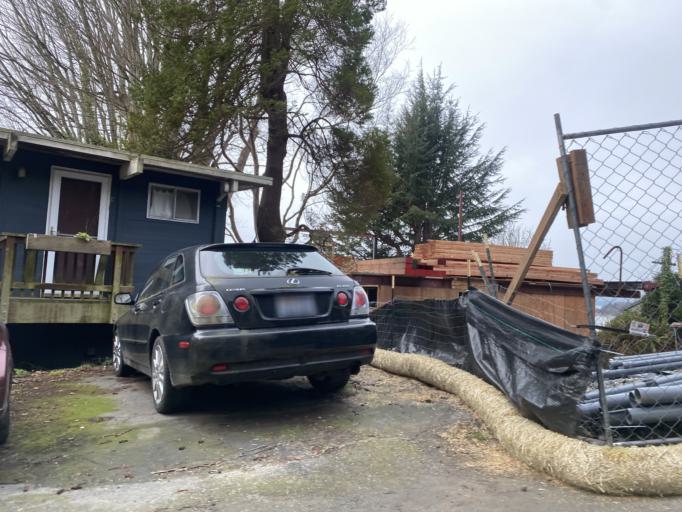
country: US
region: Washington
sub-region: King County
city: Seattle
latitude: 47.6469
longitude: -122.4163
